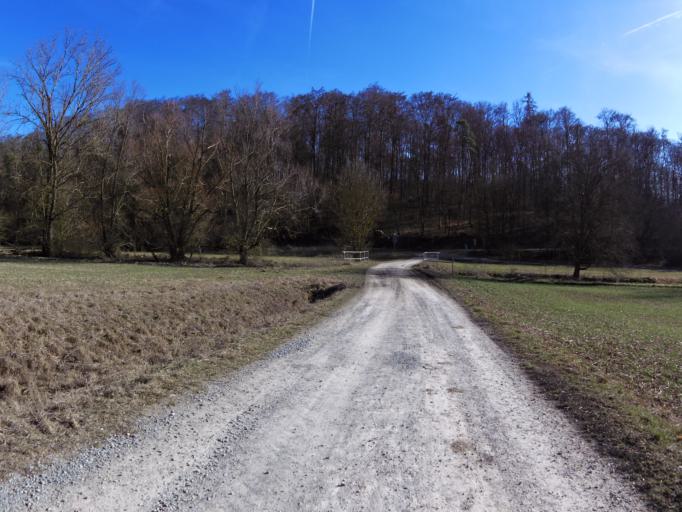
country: DE
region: Bavaria
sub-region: Regierungsbezirk Unterfranken
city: Rimpar
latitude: 49.8572
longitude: 9.9831
